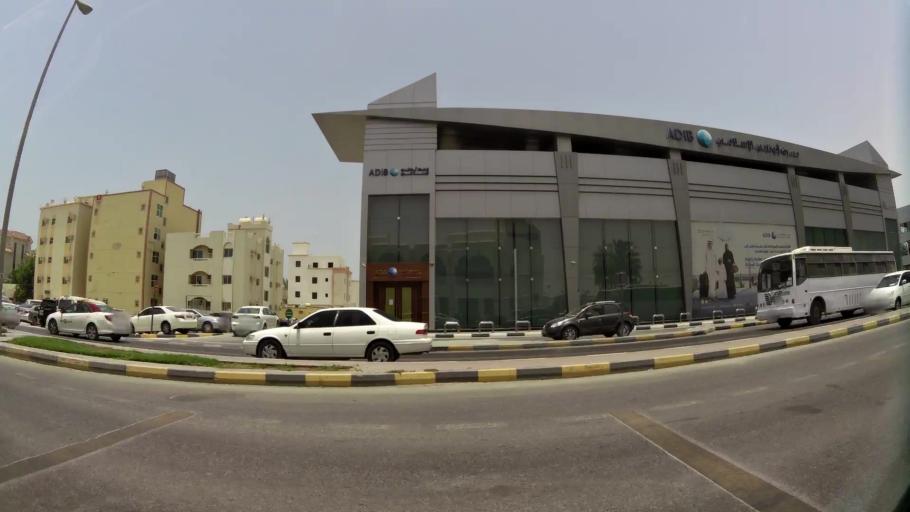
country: AE
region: Ash Shariqah
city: Sharjah
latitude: 25.3549
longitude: 55.3992
